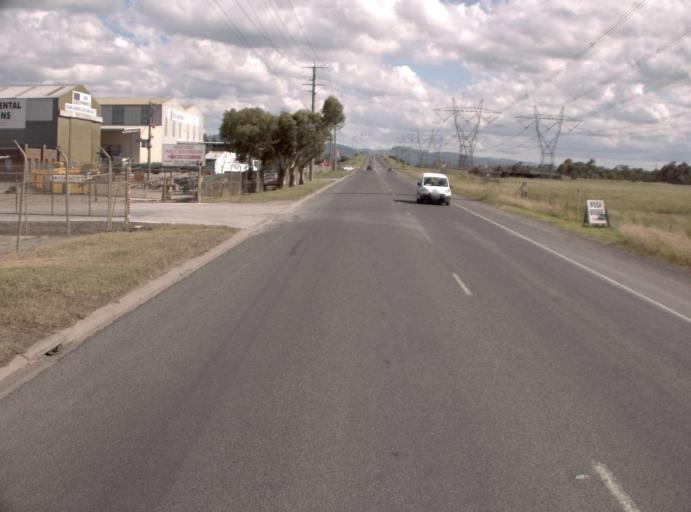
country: AU
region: Victoria
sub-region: Latrobe
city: Morwell
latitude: -38.2394
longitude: 146.4380
